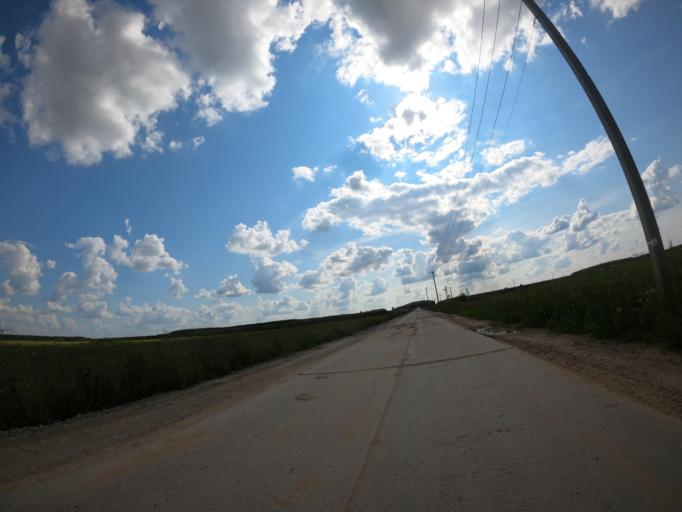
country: RU
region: Moskovskaya
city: Troitskoye
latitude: 55.2441
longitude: 38.5207
